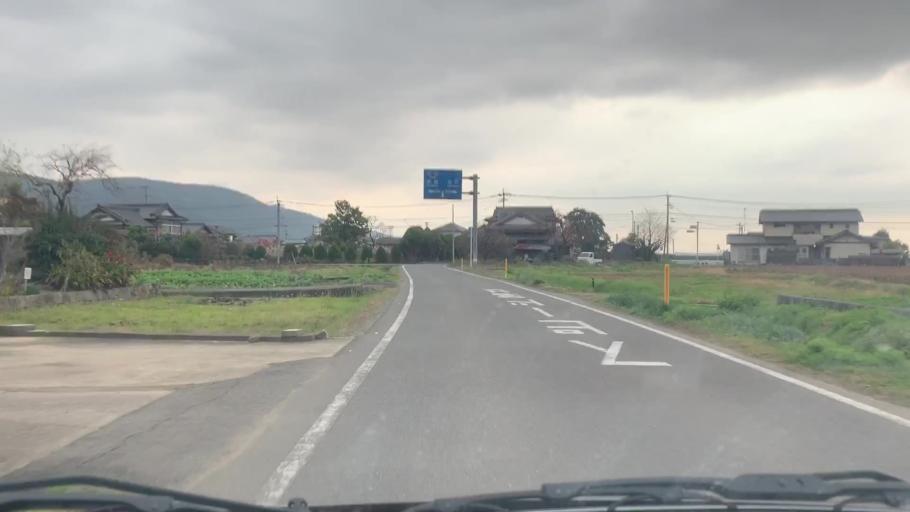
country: JP
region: Saga Prefecture
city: Kashima
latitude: 33.1214
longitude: 130.0621
